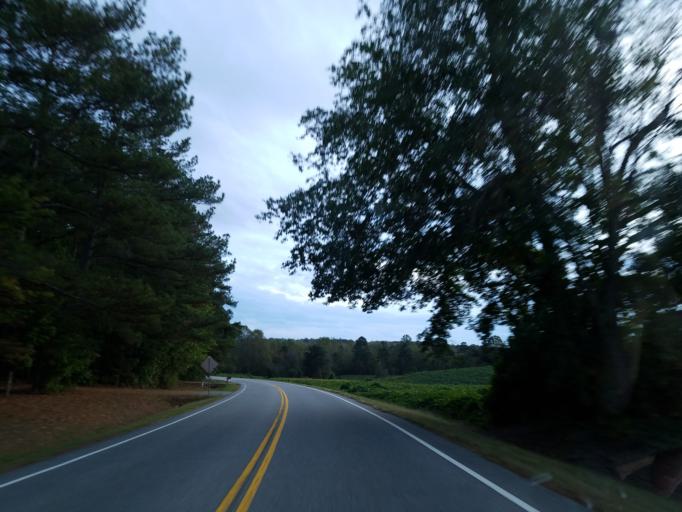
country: US
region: Georgia
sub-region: Dawson County
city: Dawsonville
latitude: 34.3912
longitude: -84.1262
